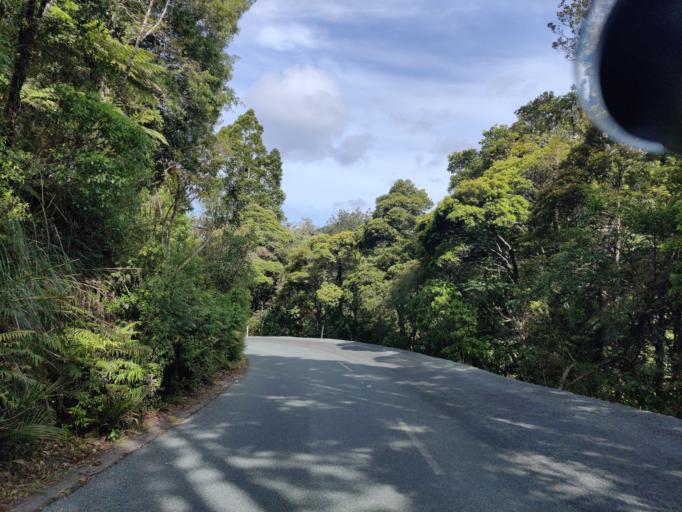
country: NZ
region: Northland
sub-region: Kaipara District
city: Dargaville
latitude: -35.6521
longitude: 173.5669
